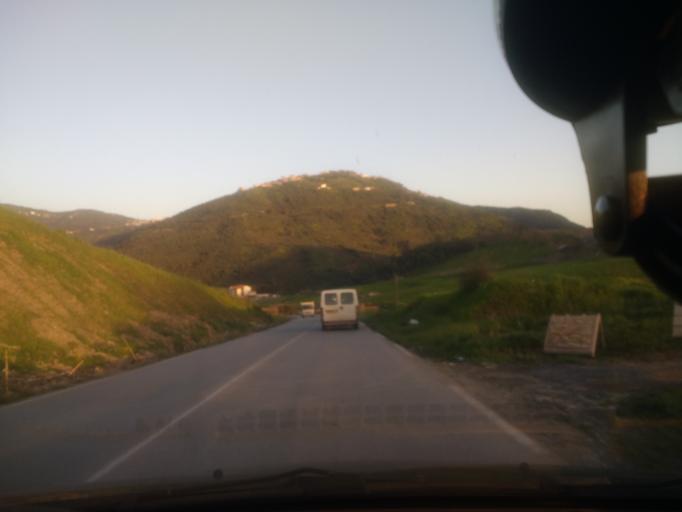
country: DZ
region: Boumerdes
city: Makouda
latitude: 36.7598
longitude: 4.0576
